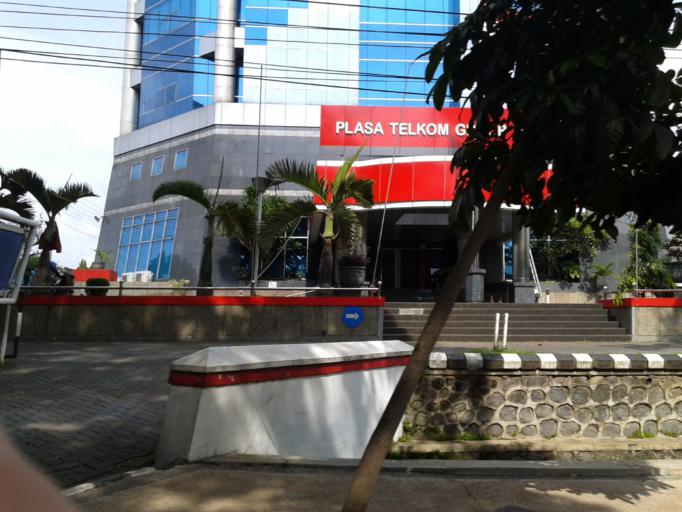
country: ID
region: East Java
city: Malang
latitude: -7.9446
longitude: 112.6427
